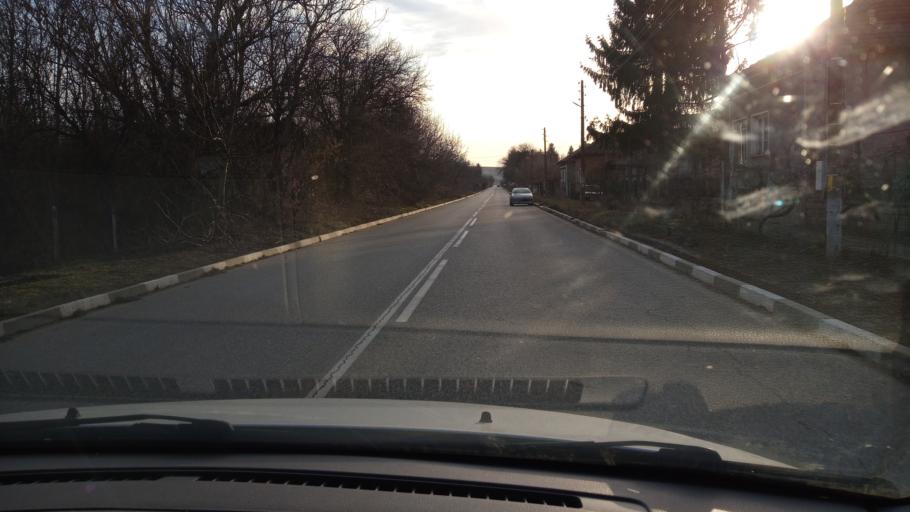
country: BG
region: Pleven
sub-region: Obshtina Pleven
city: Slavyanovo
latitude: 43.5573
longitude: 24.8671
